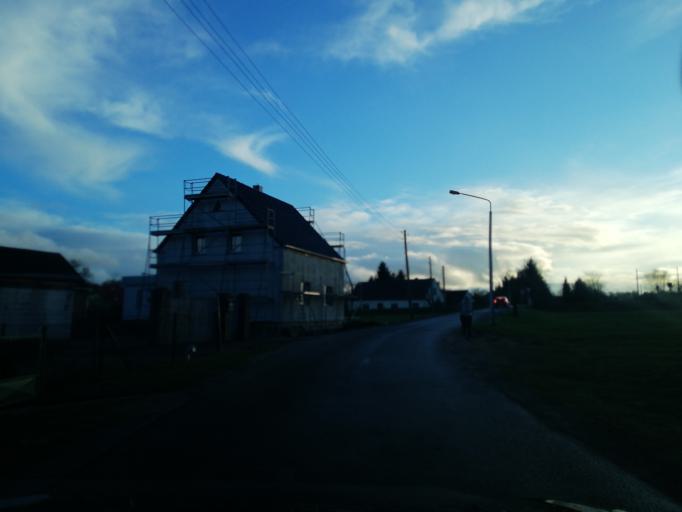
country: DE
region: Brandenburg
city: Calau
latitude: 51.7283
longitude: 13.9559
